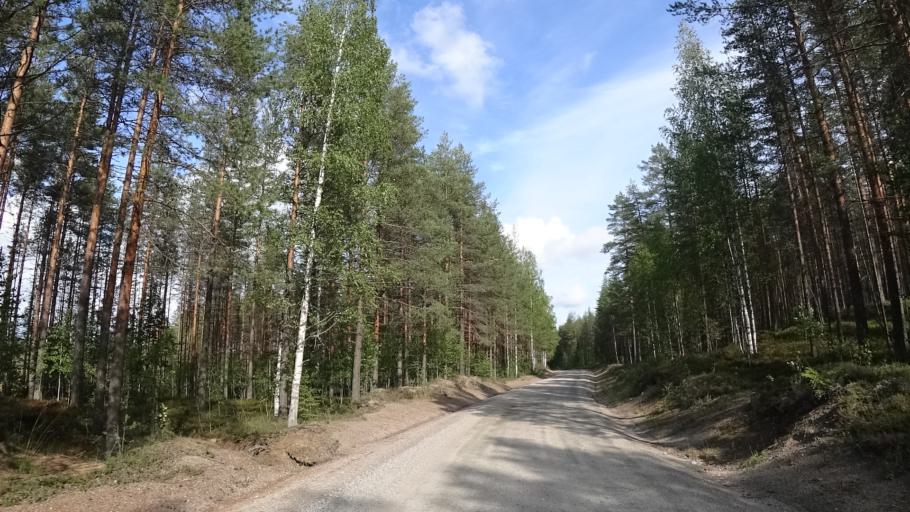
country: FI
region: North Karelia
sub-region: Pielisen Karjala
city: Lieksa
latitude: 63.5699
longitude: 30.1032
